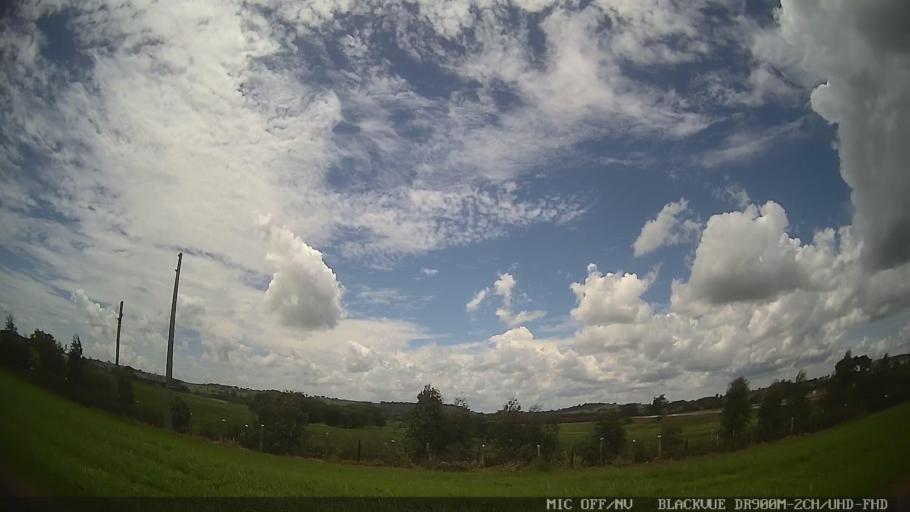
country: BR
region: Sao Paulo
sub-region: Conchas
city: Conchas
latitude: -23.0446
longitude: -47.9392
